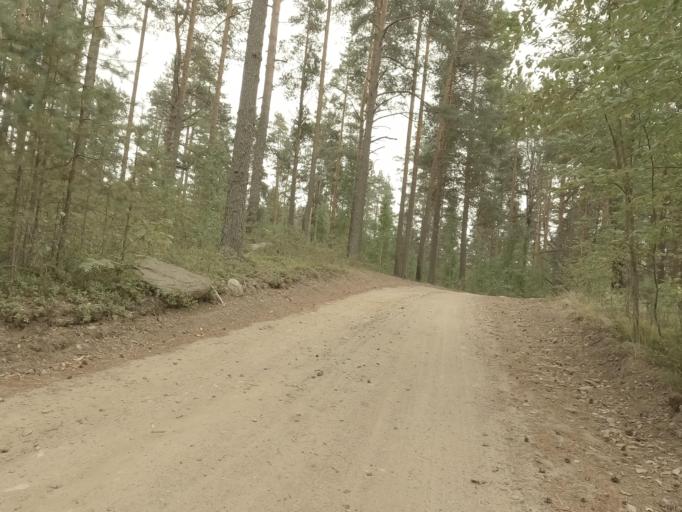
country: RU
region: Leningrad
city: Kamennogorsk
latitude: 60.9943
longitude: 29.1871
